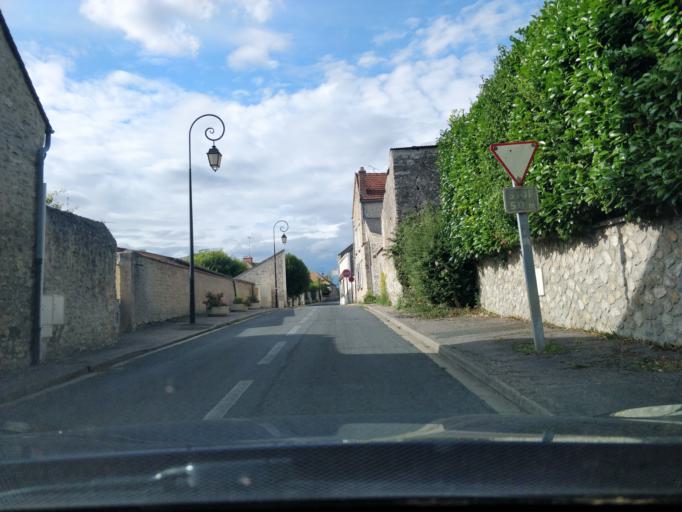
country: FR
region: Ile-de-France
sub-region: Departement de l'Essonne
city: Etampes
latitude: 48.4030
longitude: 2.1500
